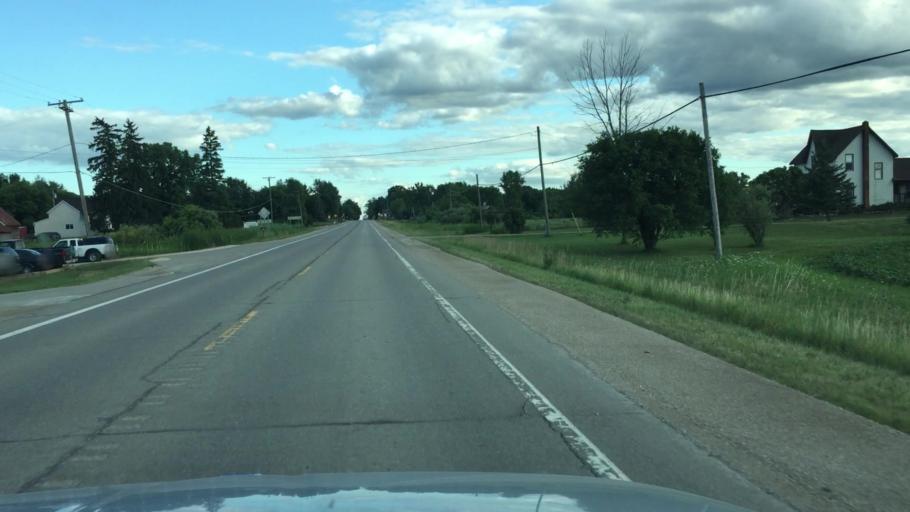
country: US
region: Michigan
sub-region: Saint Clair County
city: Yale
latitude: 43.1432
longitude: -82.7993
